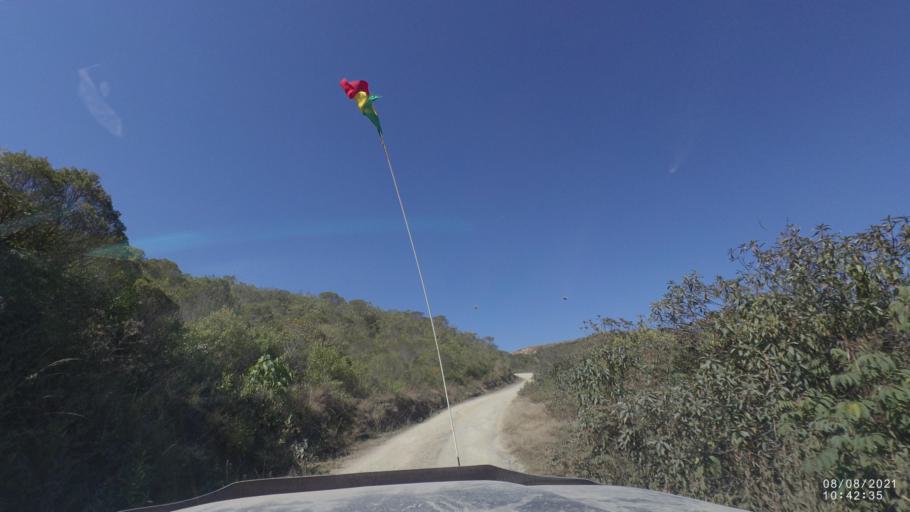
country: BO
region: La Paz
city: Quime
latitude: -16.7006
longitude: -66.7217
